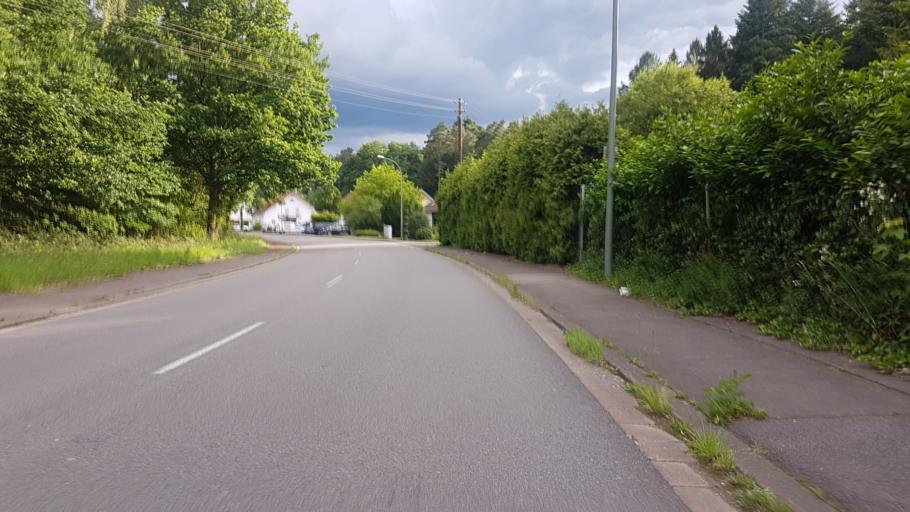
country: DE
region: Saarland
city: Britten
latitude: 49.4836
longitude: 6.6910
